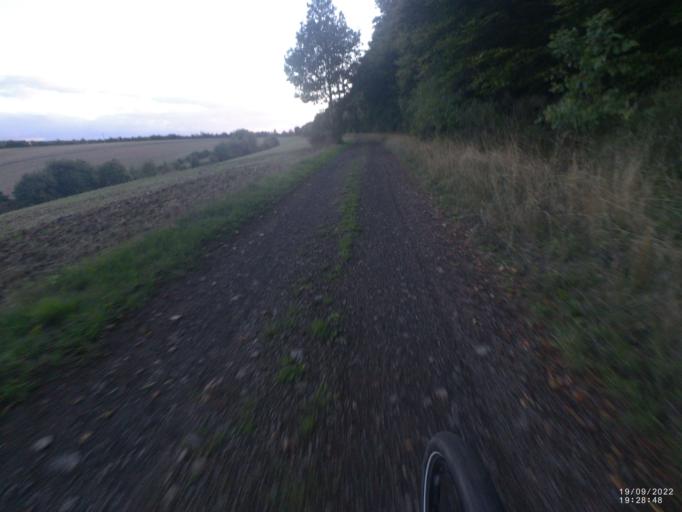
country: DE
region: Rheinland-Pfalz
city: Brockscheid
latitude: 50.1386
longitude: 6.8531
